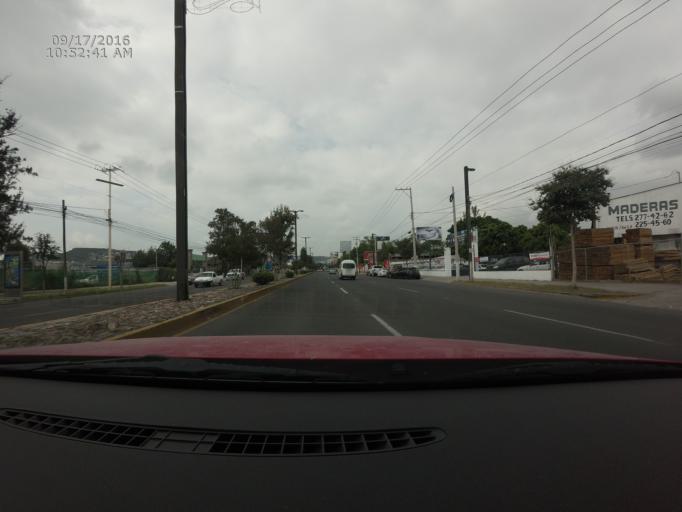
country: MX
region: Queretaro
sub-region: Corregidora
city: El Pueblito
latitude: 20.5366
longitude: -100.4356
